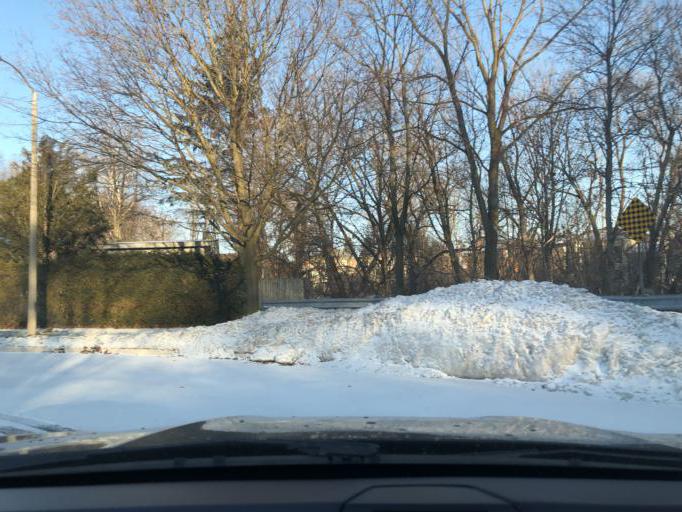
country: CA
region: Ontario
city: Scarborough
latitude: 43.7781
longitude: -79.1494
